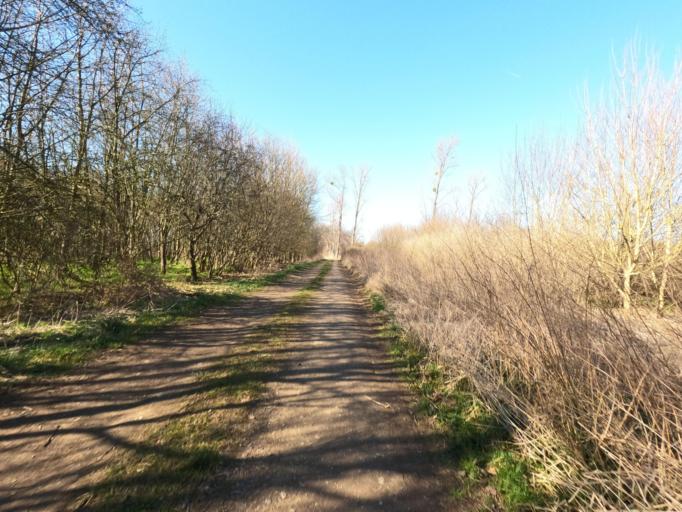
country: DE
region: North Rhine-Westphalia
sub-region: Regierungsbezirk Koln
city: Linnich
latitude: 50.9721
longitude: 6.2980
